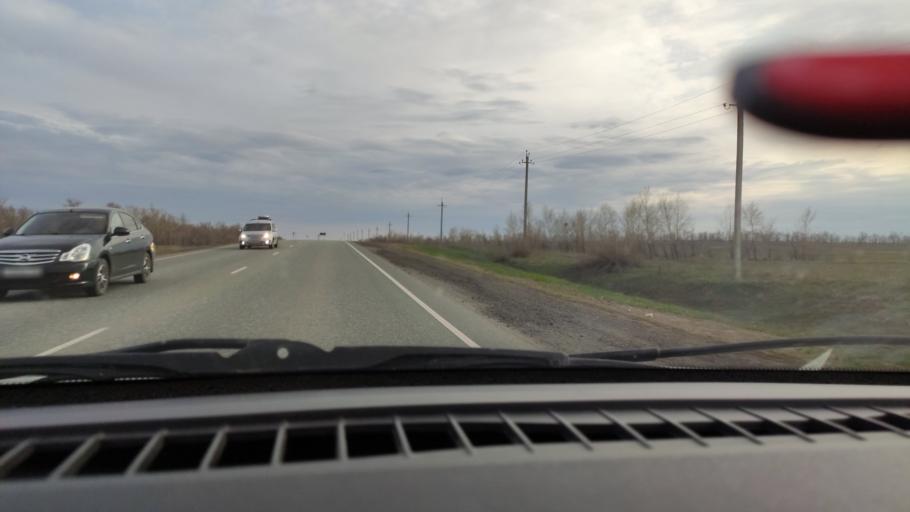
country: RU
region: Orenburg
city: Tatarskaya Kargala
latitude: 52.0044
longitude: 55.1999
